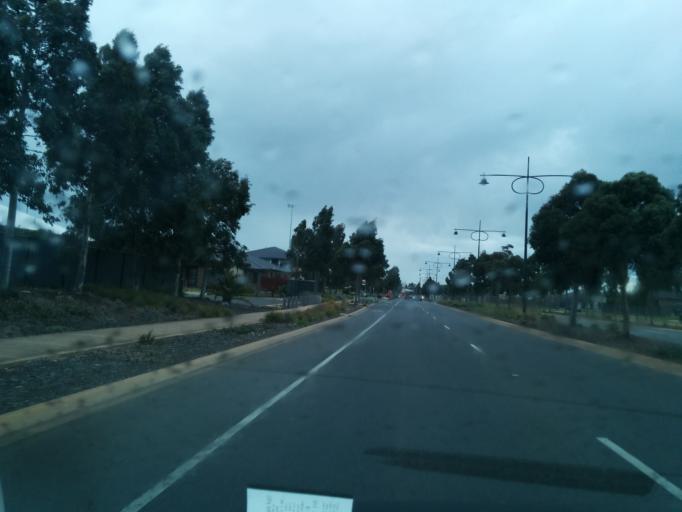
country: AU
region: Victoria
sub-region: Wyndham
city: Point Cook
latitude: -37.8970
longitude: 144.7281
